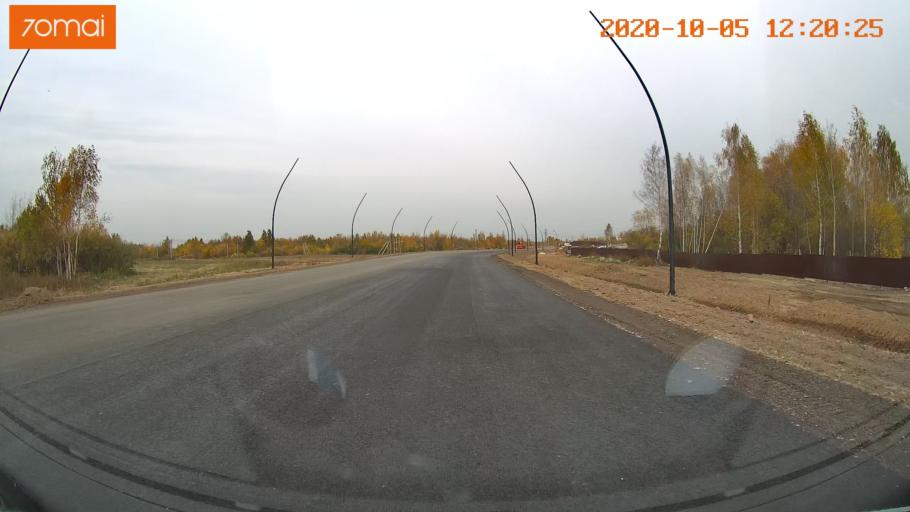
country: RU
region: Ivanovo
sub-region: Gorod Ivanovo
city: Ivanovo
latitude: 56.9633
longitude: 40.9307
